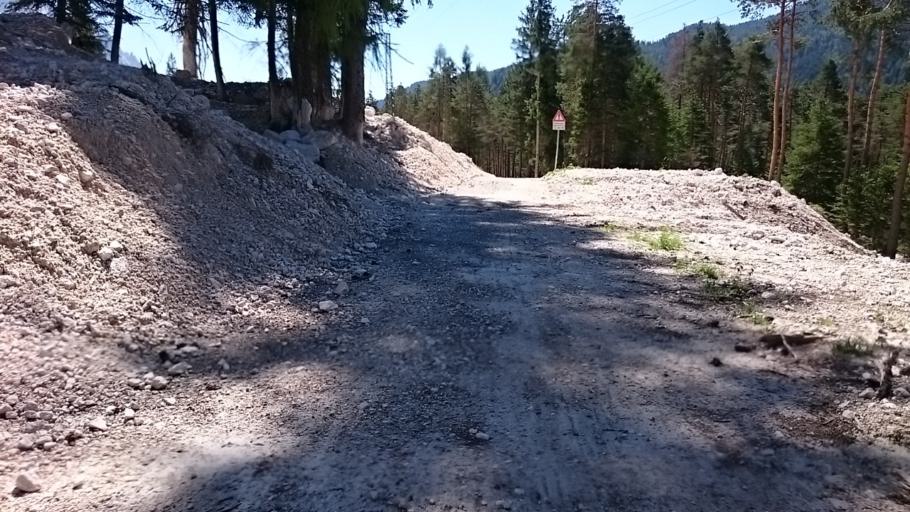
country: IT
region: Veneto
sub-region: Provincia di Belluno
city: Cortina d'Ampezzo
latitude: 46.5014
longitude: 12.1651
